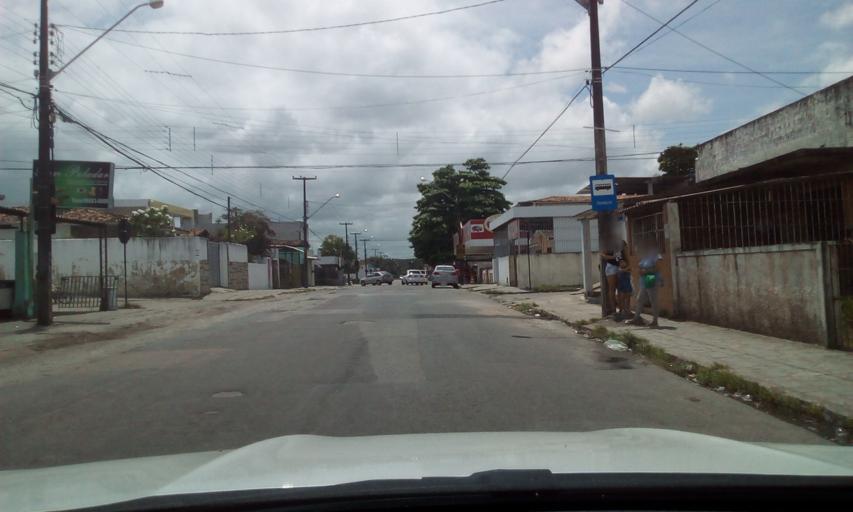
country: BR
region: Paraiba
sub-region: Bayeux
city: Bayeux
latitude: -7.1802
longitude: -34.8965
